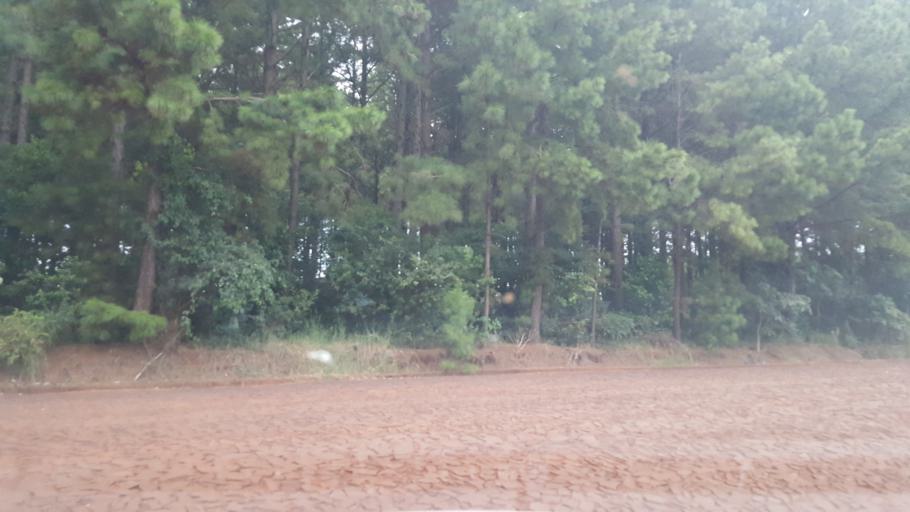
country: AR
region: Misiones
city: Capiovi
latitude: -26.9348
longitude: -55.0440
